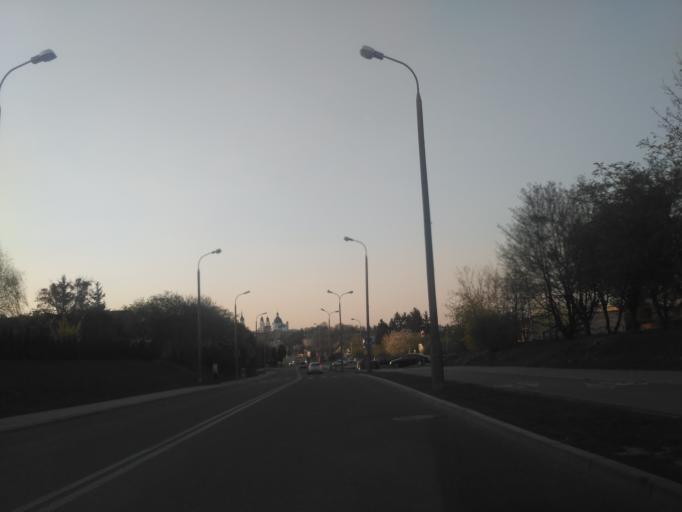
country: PL
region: Lublin Voivodeship
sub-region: Chelm
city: Chelm
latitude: 51.1229
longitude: 23.4833
